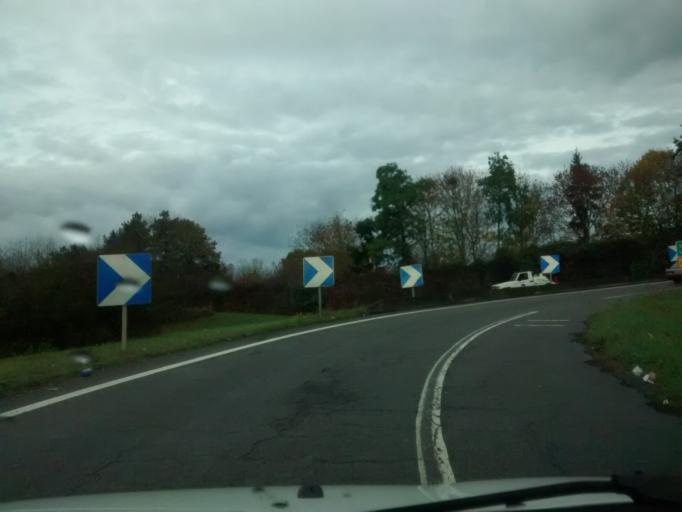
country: FR
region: Brittany
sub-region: Departement d'Ille-et-Vilaine
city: Chantepie
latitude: 48.0829
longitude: -1.6450
